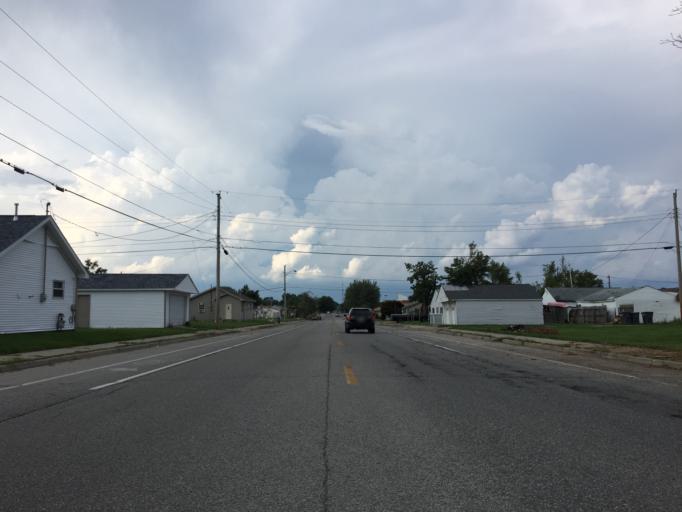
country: US
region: Indiana
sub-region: Howard County
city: Kokomo
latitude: 40.4672
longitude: -86.1109
